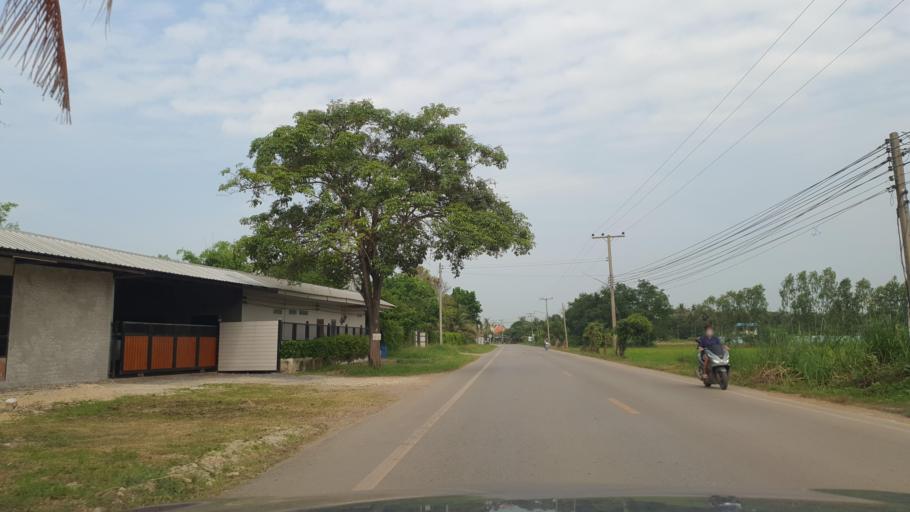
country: TH
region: Phitsanulok
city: Bang Rakam
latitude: 16.8143
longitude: 100.1690
